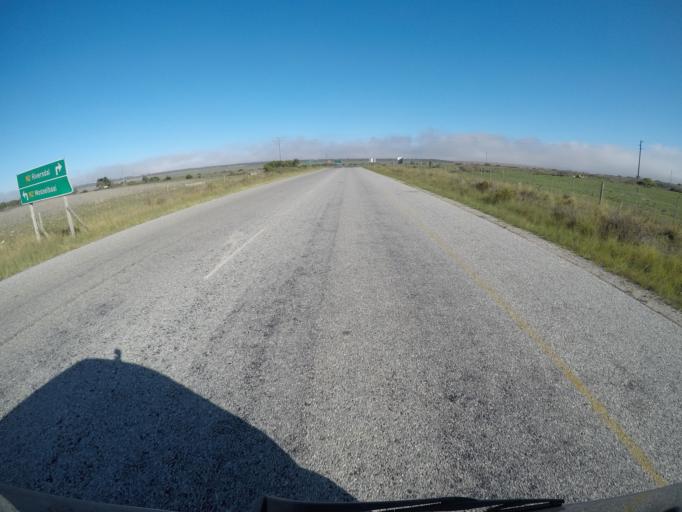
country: ZA
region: Western Cape
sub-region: Eden District Municipality
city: Mossel Bay
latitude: -34.1793
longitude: 22.0170
